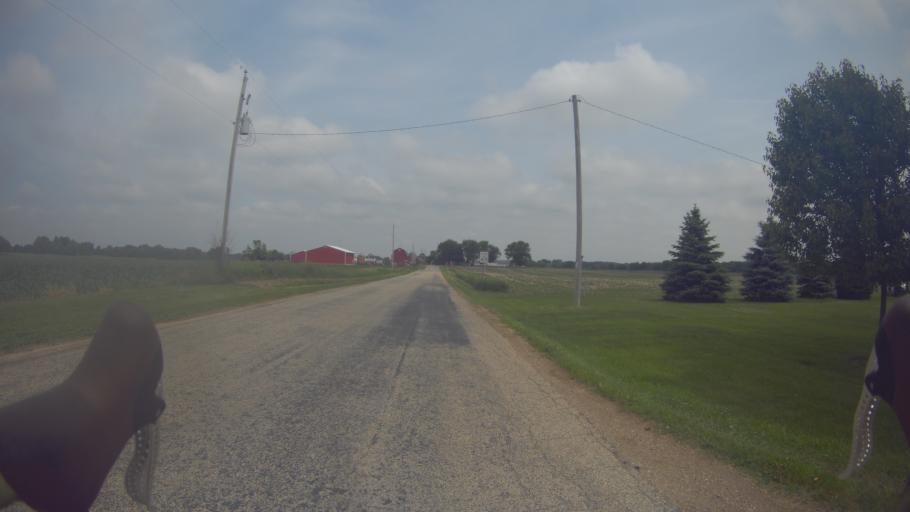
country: US
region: Wisconsin
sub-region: Jefferson County
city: Lake Ripley
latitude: 42.9394
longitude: -88.9889
